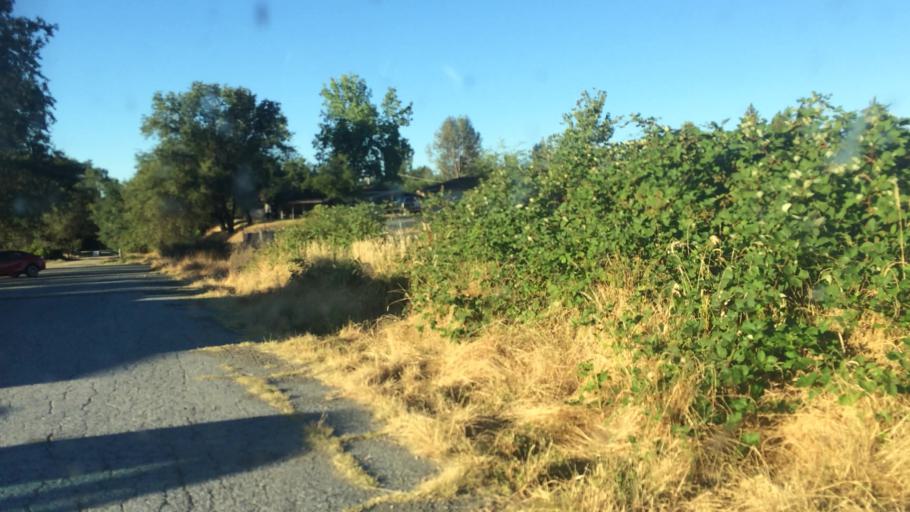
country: US
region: California
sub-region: El Dorado County
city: Diamond Springs
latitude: 38.6928
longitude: -120.8185
